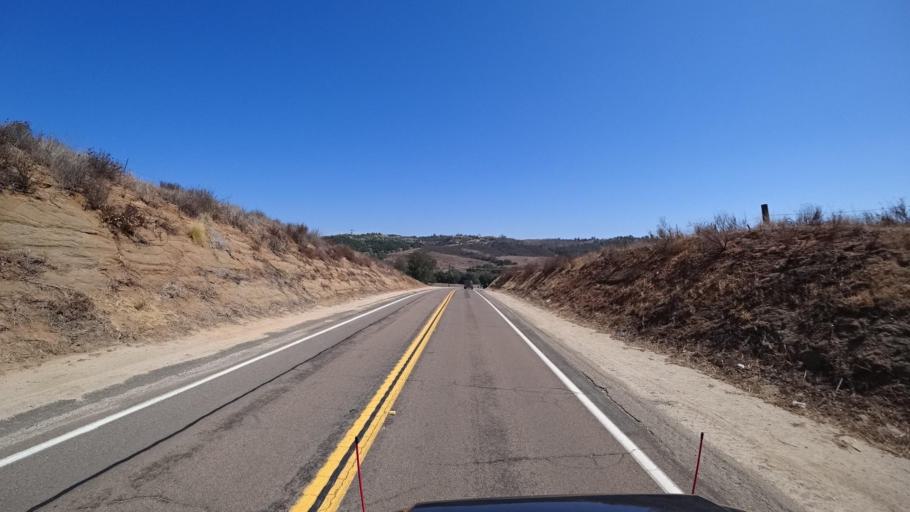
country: US
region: California
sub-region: San Diego County
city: Hidden Meadows
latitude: 33.2910
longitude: -117.0847
